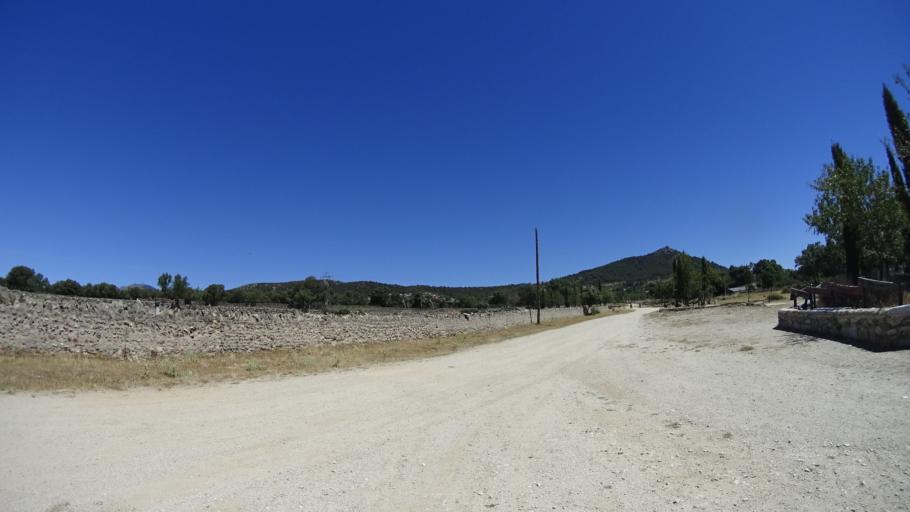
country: ES
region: Madrid
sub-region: Provincia de Madrid
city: Collado Mediano
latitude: 40.6847
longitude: -4.0355
